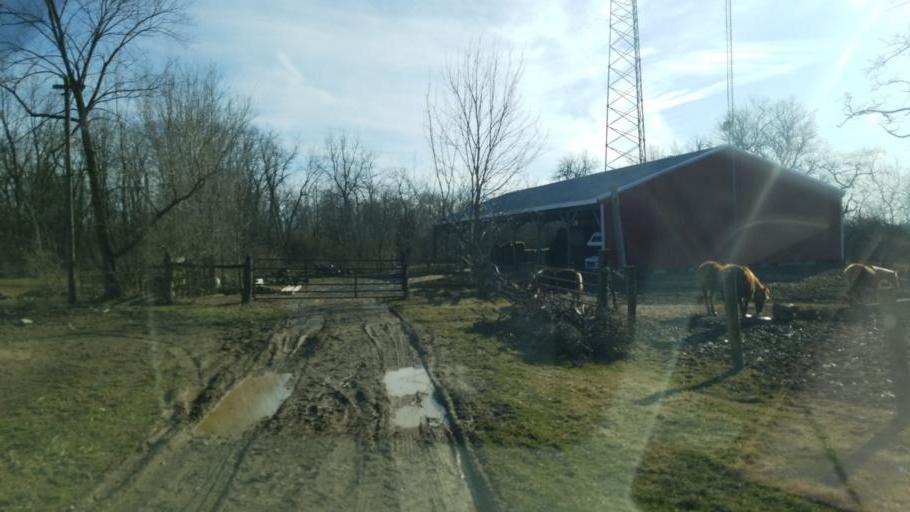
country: US
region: Ohio
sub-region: Logan County
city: Bellefontaine
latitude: 40.3362
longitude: -83.6620
